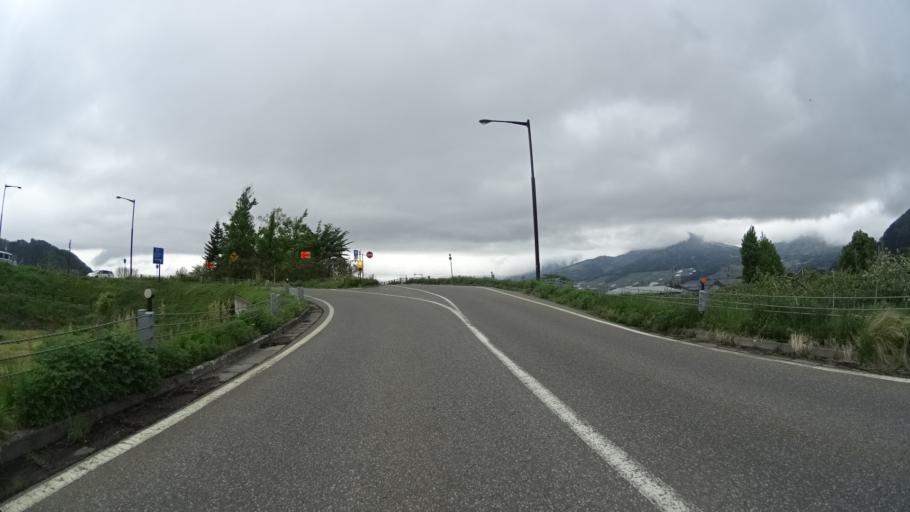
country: JP
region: Nagano
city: Nakano
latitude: 36.7429
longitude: 138.4044
